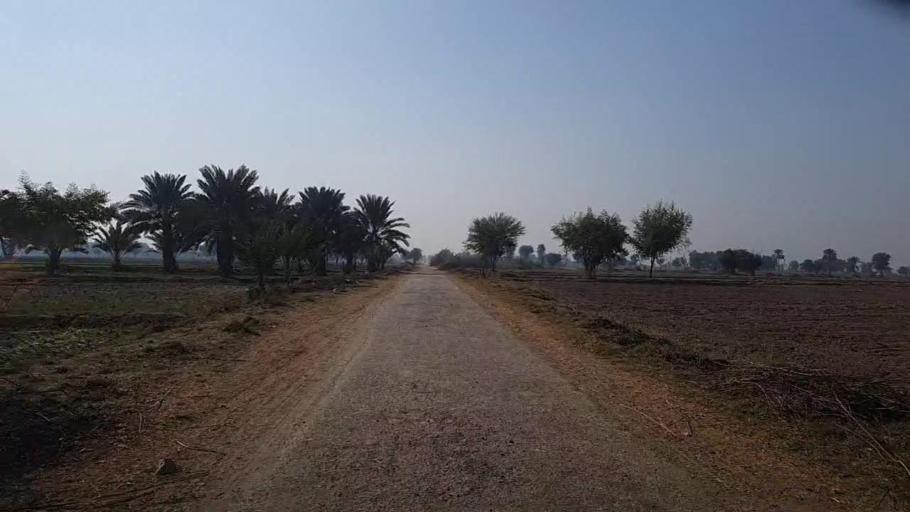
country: PK
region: Sindh
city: Bozdar
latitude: 27.2489
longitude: 68.6087
